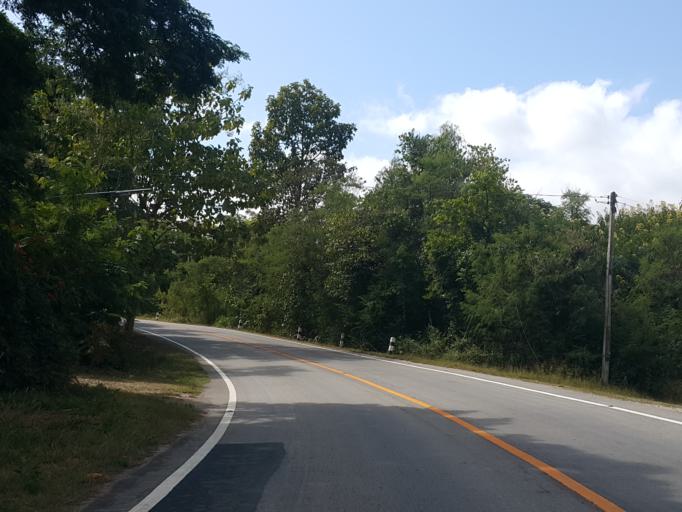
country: TH
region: Chiang Mai
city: San Kamphaeng
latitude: 18.7187
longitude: 99.1769
